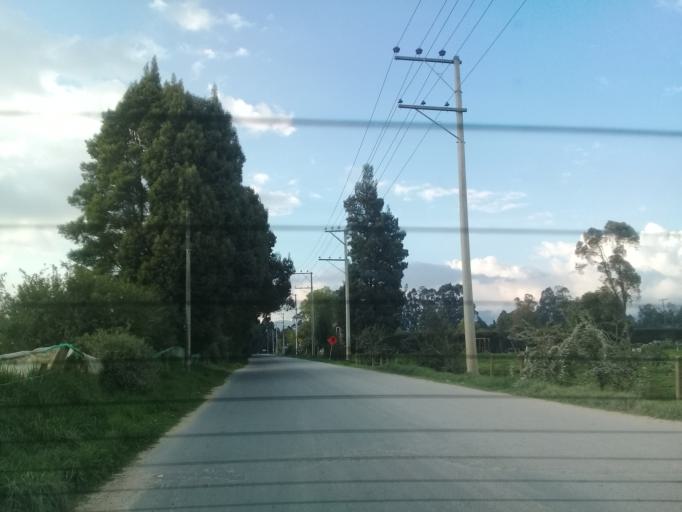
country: CO
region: Cundinamarca
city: Madrid
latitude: 4.7824
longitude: -74.2695
